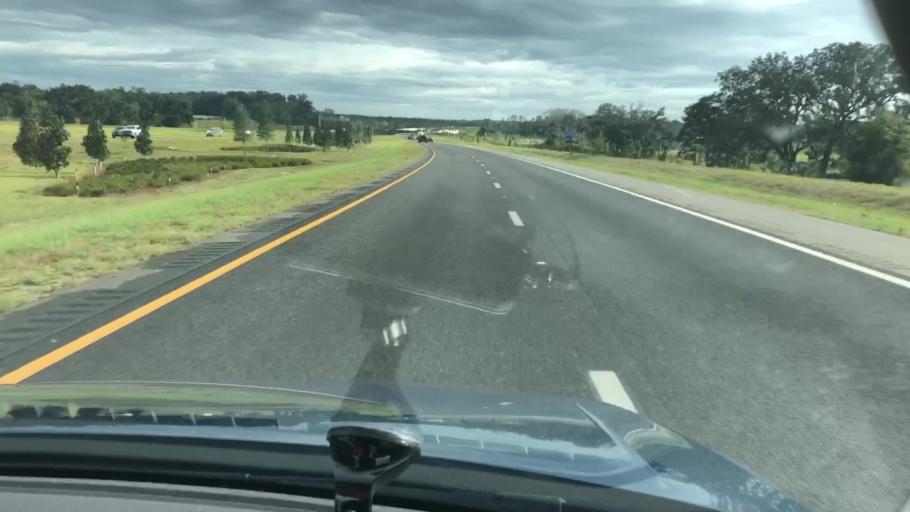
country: US
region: Florida
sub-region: Orange County
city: Zellwood
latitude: 28.7416
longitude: -81.5665
